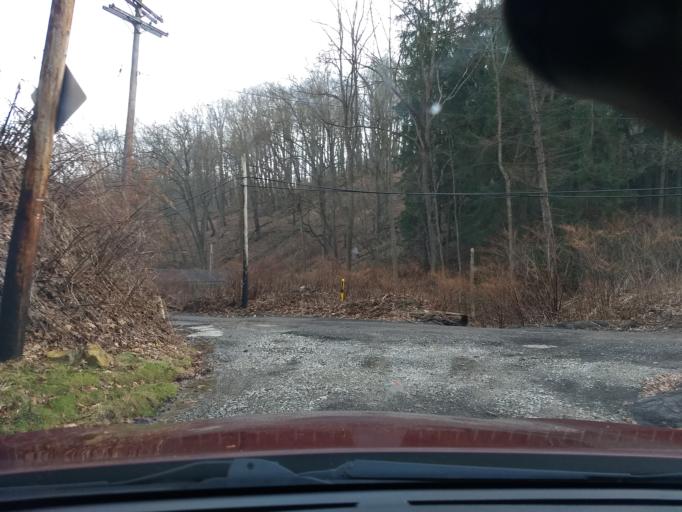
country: US
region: Pennsylvania
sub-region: Allegheny County
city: Brentwood
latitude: 40.3711
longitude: -79.9637
